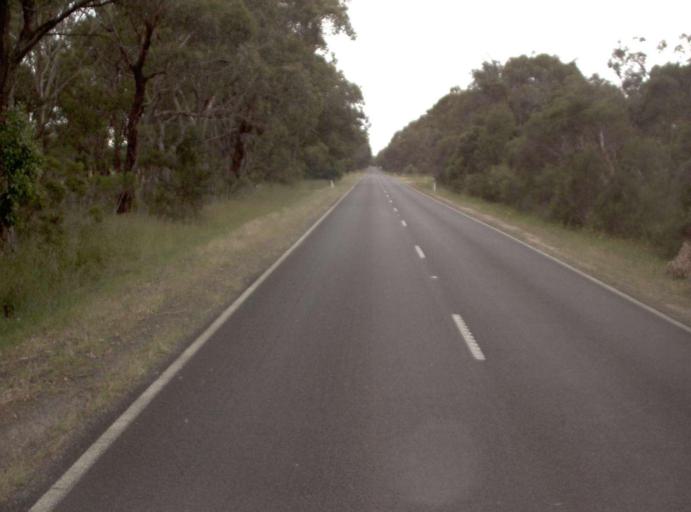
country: AU
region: Victoria
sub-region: Latrobe
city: Traralgon
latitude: -38.5333
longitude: 146.8562
